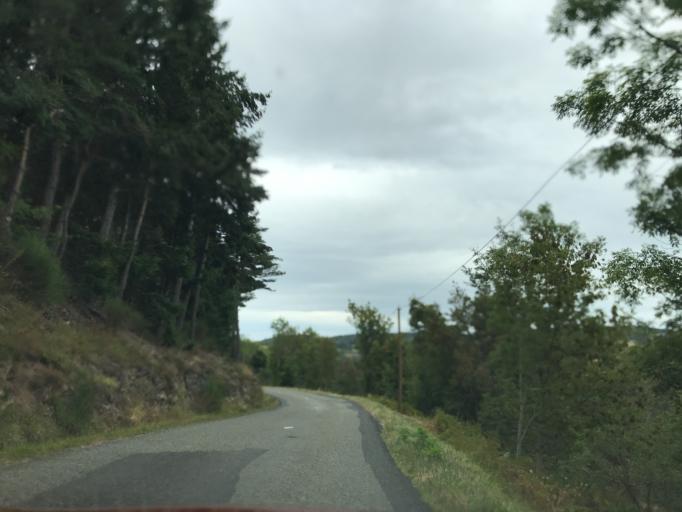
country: FR
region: Rhone-Alpes
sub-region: Departement de la Loire
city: Sail-sous-Couzan
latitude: 45.6927
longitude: 3.9193
